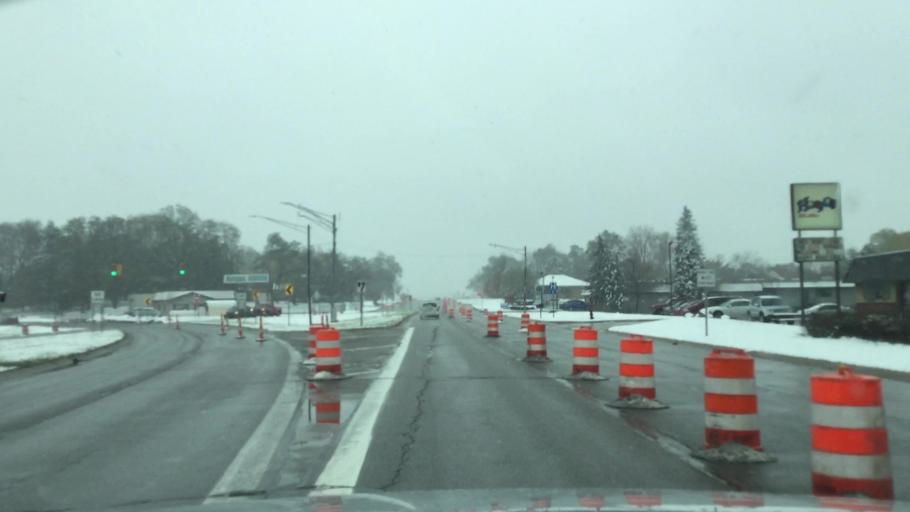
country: US
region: Michigan
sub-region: Oakland County
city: Auburn Hills
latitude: 42.6823
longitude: -83.2453
